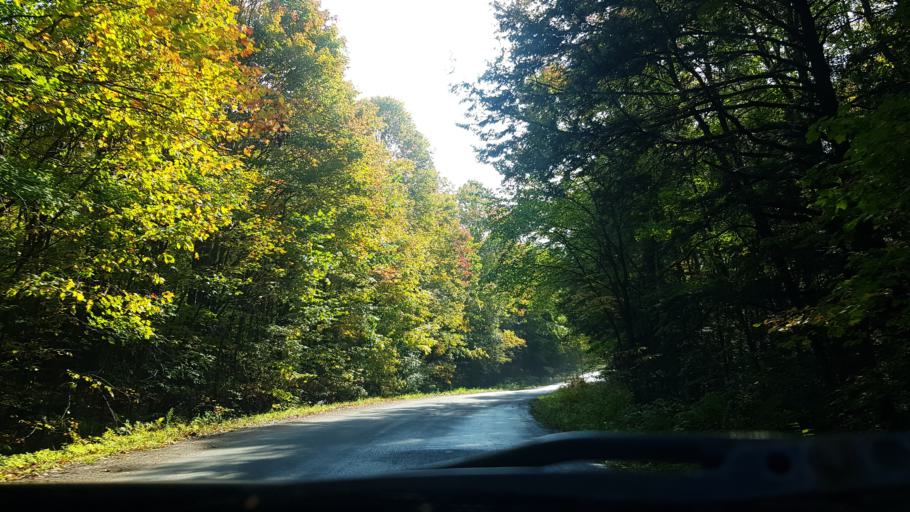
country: CA
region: Ontario
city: Bracebridge
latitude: 44.9584
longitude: -79.2512
